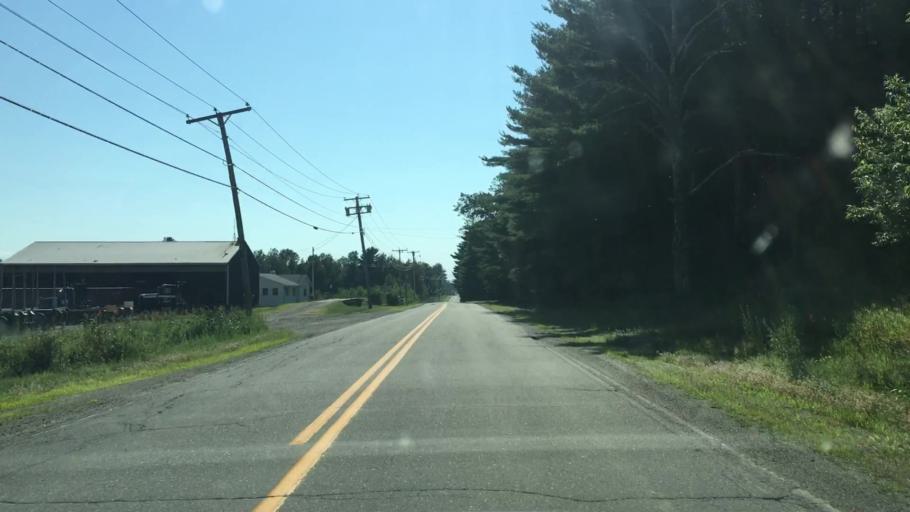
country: US
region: Maine
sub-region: Penobscot County
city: Enfield
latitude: 45.2471
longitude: -68.5956
